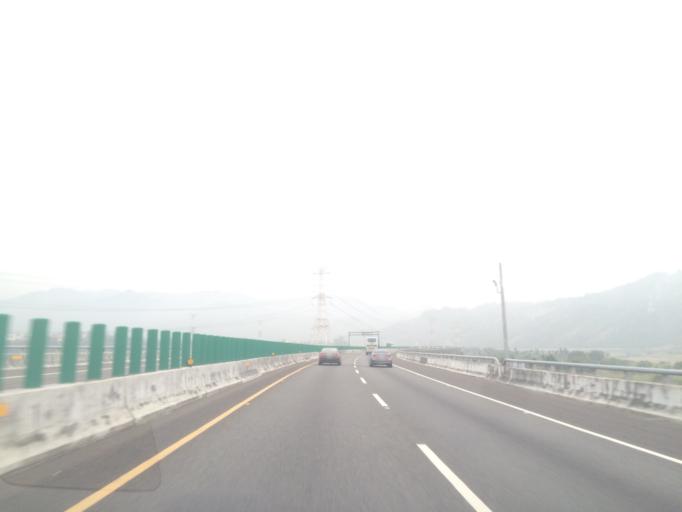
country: TW
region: Taiwan
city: Zhongxing New Village
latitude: 23.9938
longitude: 120.7506
